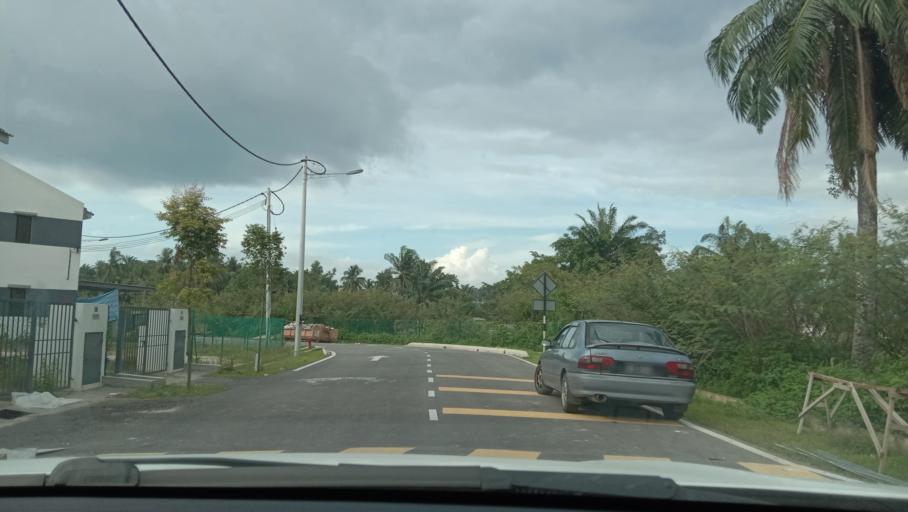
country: MY
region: Selangor
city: Ladang Seri Kundang
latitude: 3.2355
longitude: 101.4792
